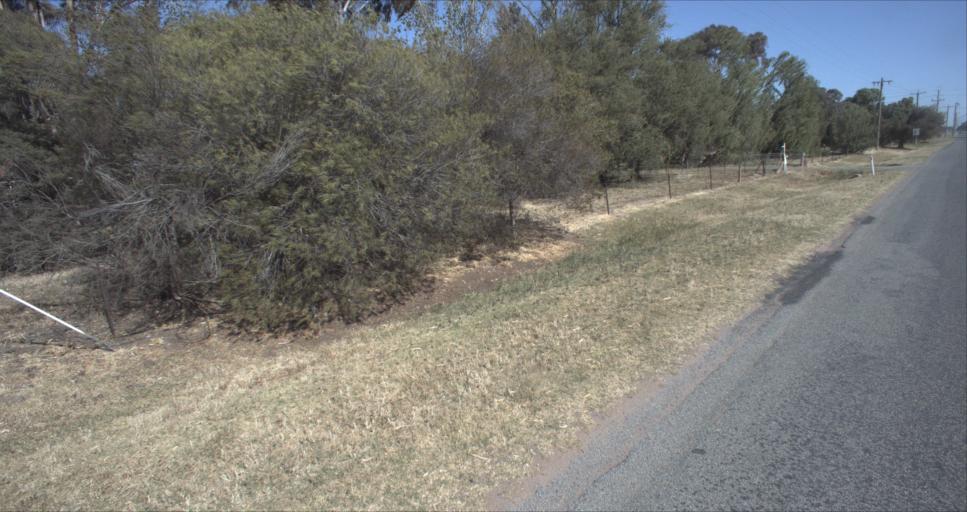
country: AU
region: New South Wales
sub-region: Leeton
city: Leeton
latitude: -34.5421
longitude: 146.4189
